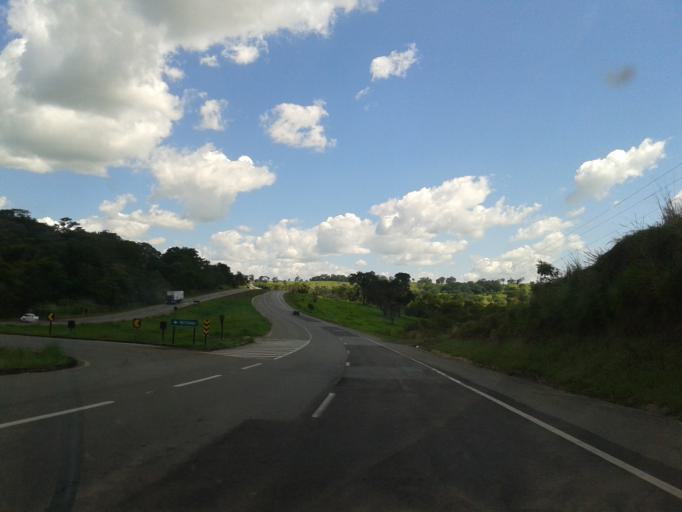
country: BR
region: Goias
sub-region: Pontalina
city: Pontalina
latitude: -17.4664
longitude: -49.2193
